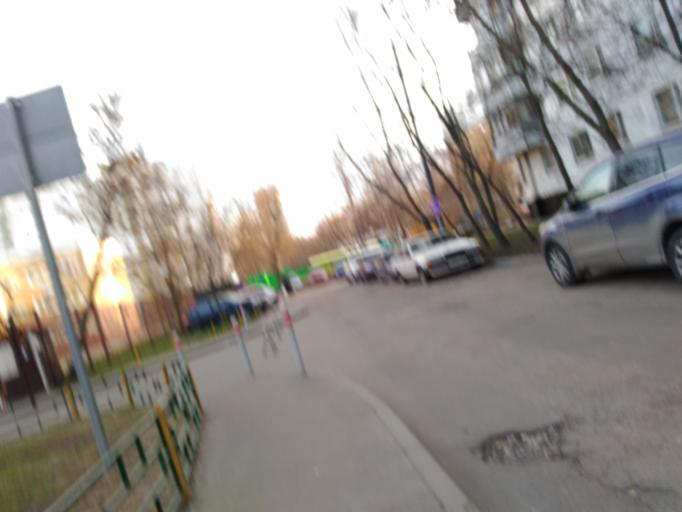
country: RU
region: Moskovskaya
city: Khoroshevo-Mnevniki
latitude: 55.7879
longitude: 37.4702
